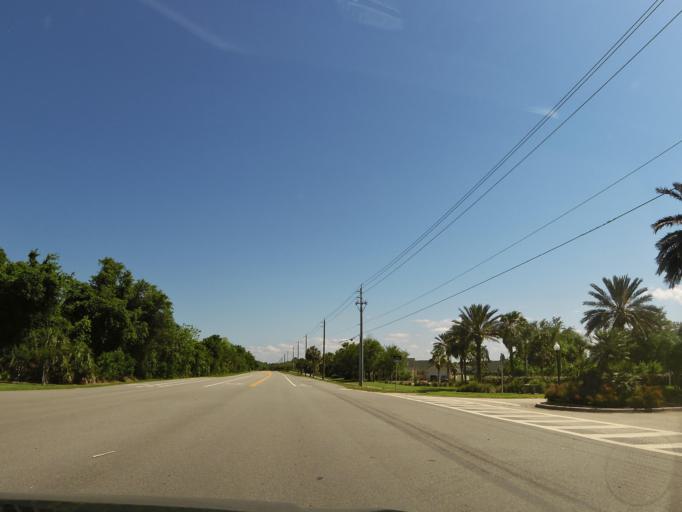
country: US
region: Florida
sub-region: Flagler County
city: Flagler Beach
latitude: 29.4237
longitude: -81.1508
